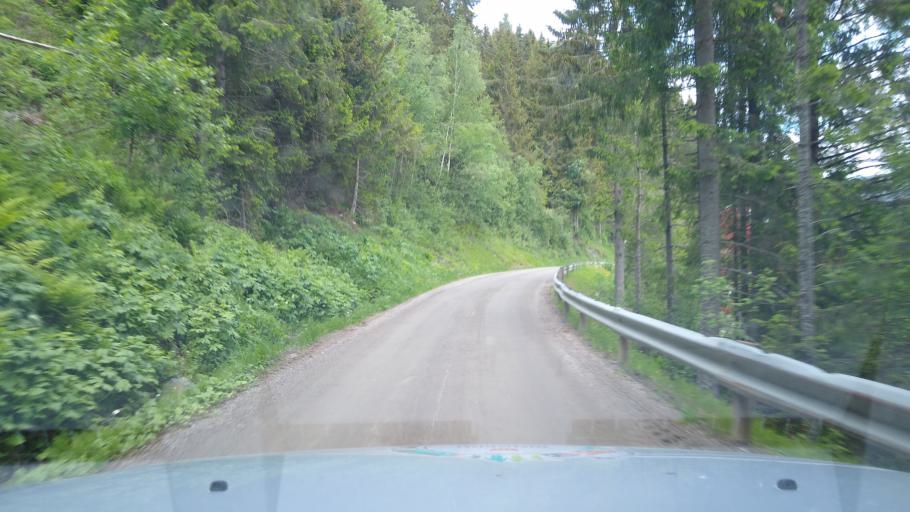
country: NO
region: Oppland
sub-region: Ringebu
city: Ringebu
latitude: 61.5011
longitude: 10.1400
